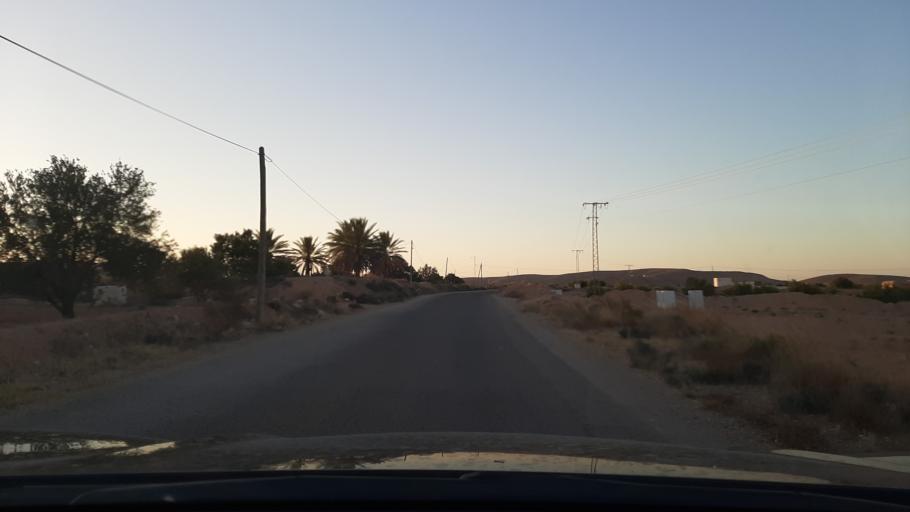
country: TN
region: Qabis
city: Matmata
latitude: 33.5580
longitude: 10.1839
